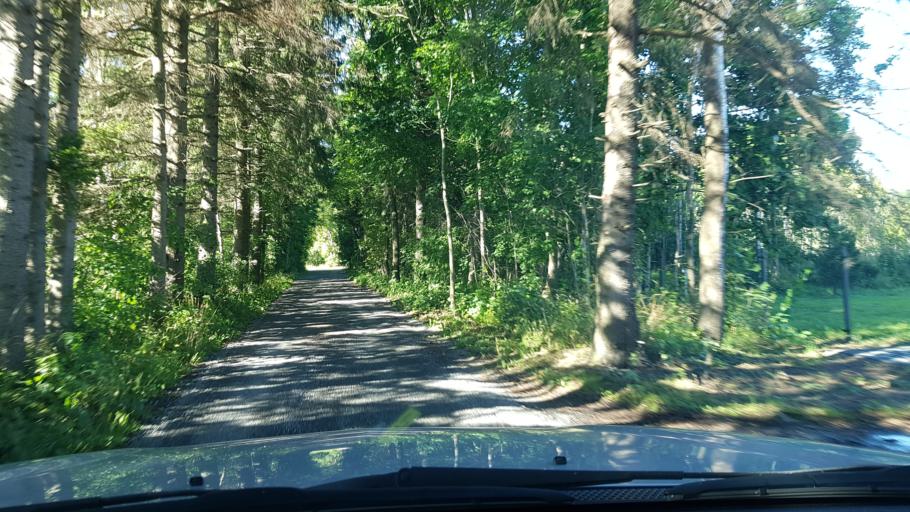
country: EE
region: Harju
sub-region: Joelaehtme vald
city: Loo
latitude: 59.4311
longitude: 24.9308
